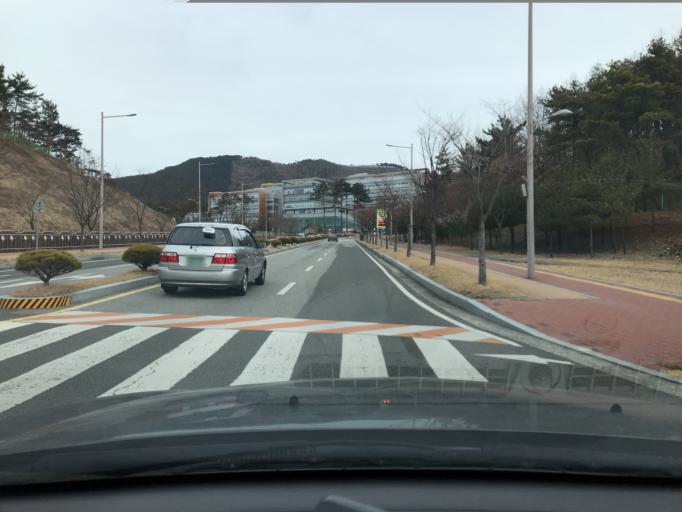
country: KR
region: Daegu
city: Hwawon
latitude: 35.7017
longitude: 128.4585
